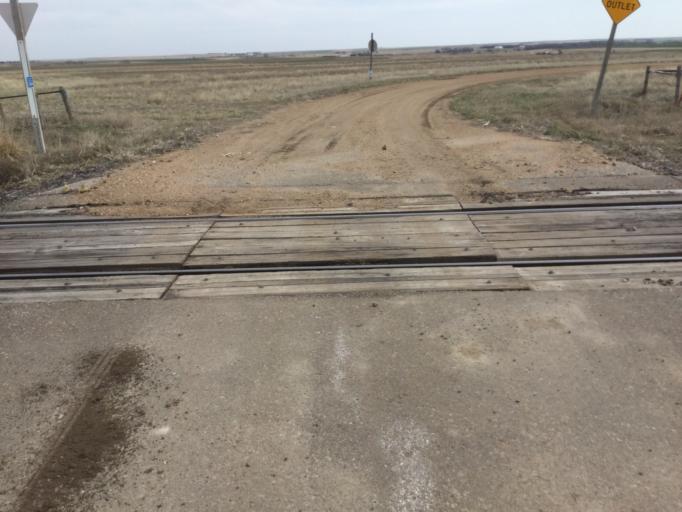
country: US
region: Kansas
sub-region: Ellis County
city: Ellis
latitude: 38.9829
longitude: -99.7142
